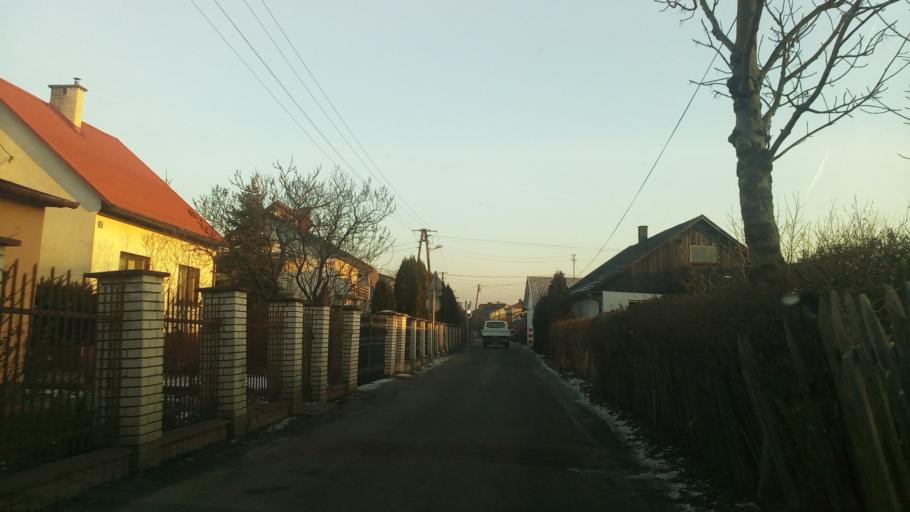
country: PL
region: Lesser Poland Voivodeship
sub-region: Powiat nowosadecki
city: Chelmiec
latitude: 49.6298
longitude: 20.6647
